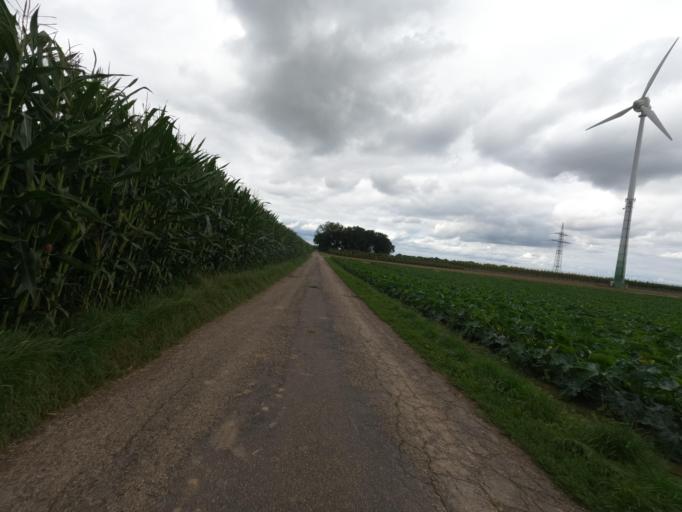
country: DE
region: North Rhine-Westphalia
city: Huckelhoven
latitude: 51.0084
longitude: 6.2167
